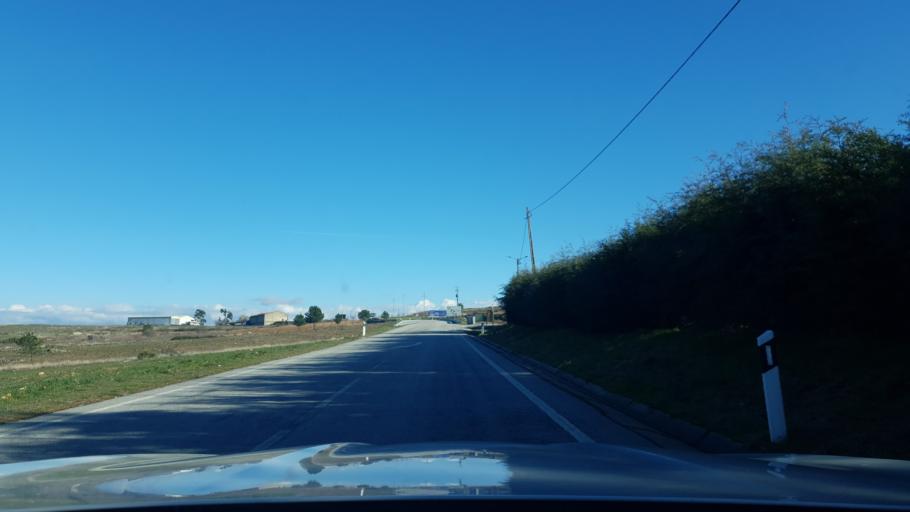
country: PT
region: Braganca
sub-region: Freixo de Espada A Cinta
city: Freixo de Espada a Cinta
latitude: 41.1789
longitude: -6.7970
